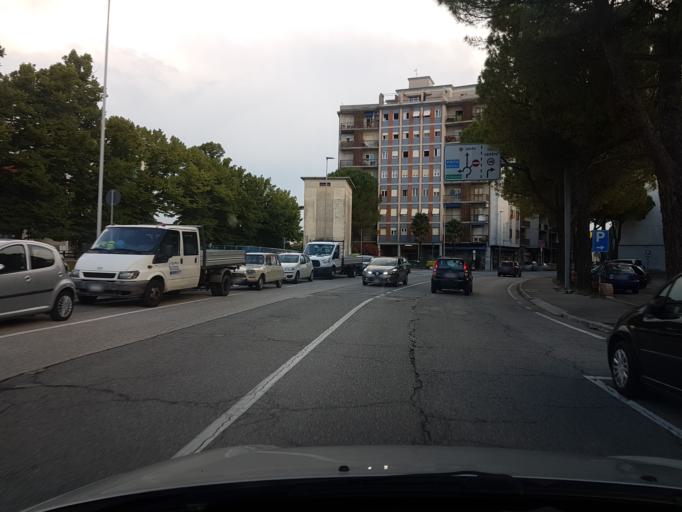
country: IT
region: Friuli Venezia Giulia
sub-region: Provincia di Gorizia
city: Monfalcone
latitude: 45.8082
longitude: 13.5255
